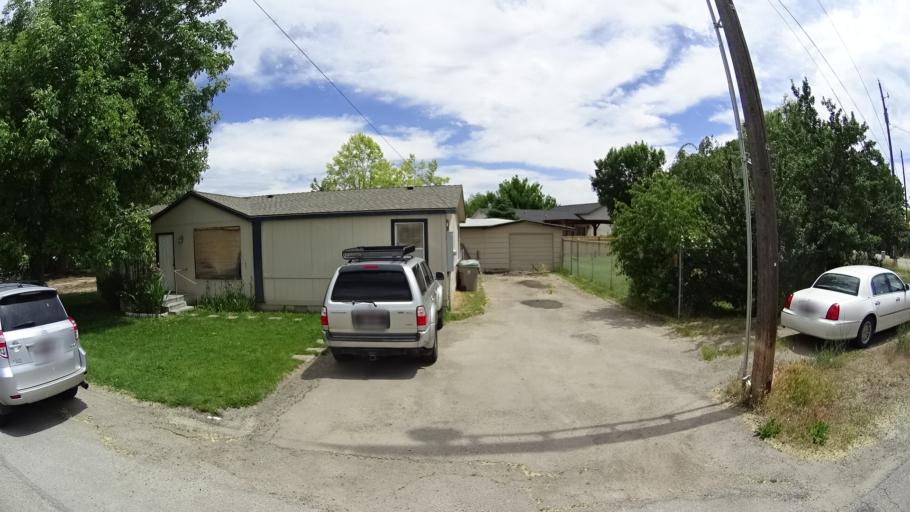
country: US
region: Idaho
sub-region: Ada County
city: Meridian
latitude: 43.6269
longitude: -116.3218
